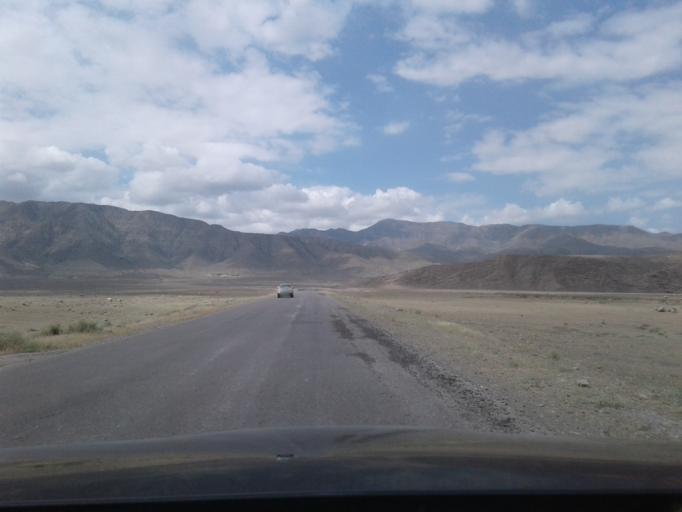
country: TM
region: Ahal
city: Baharly
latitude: 38.5130
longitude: 57.1323
